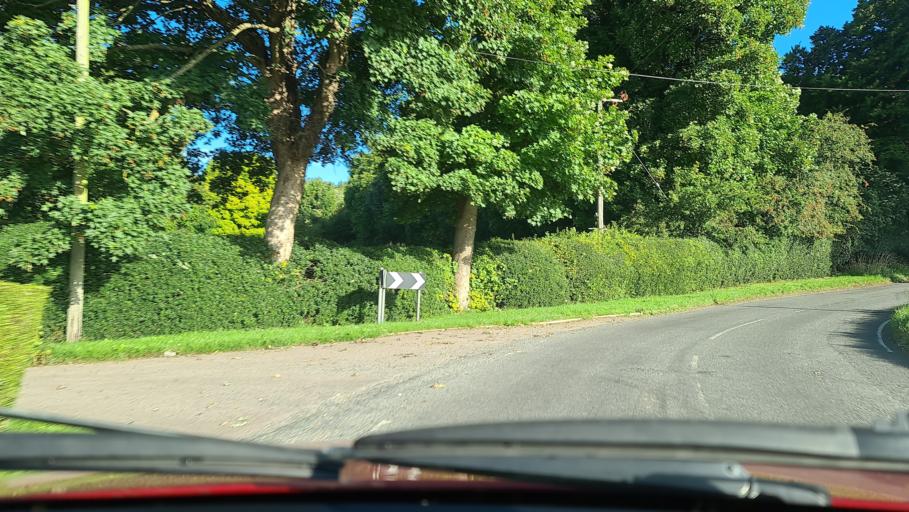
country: GB
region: England
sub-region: Oxfordshire
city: Chinnor
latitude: 51.6945
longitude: -0.8688
